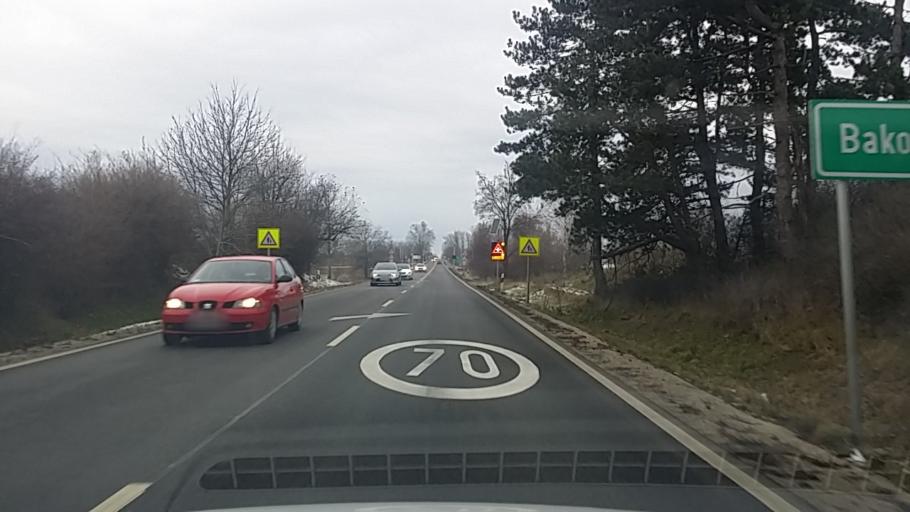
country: HU
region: Komarom-Esztergom
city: Csaszar
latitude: 47.4467
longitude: 18.1075
